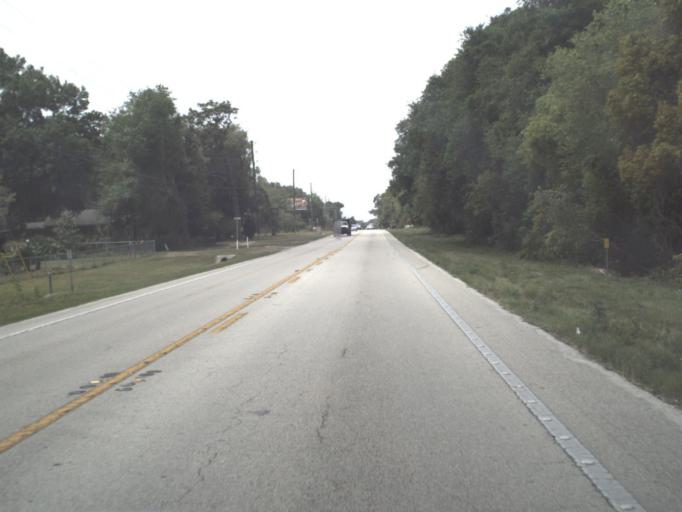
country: US
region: Florida
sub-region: Lake County
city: Mount Dora
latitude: 28.8517
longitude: -81.6232
